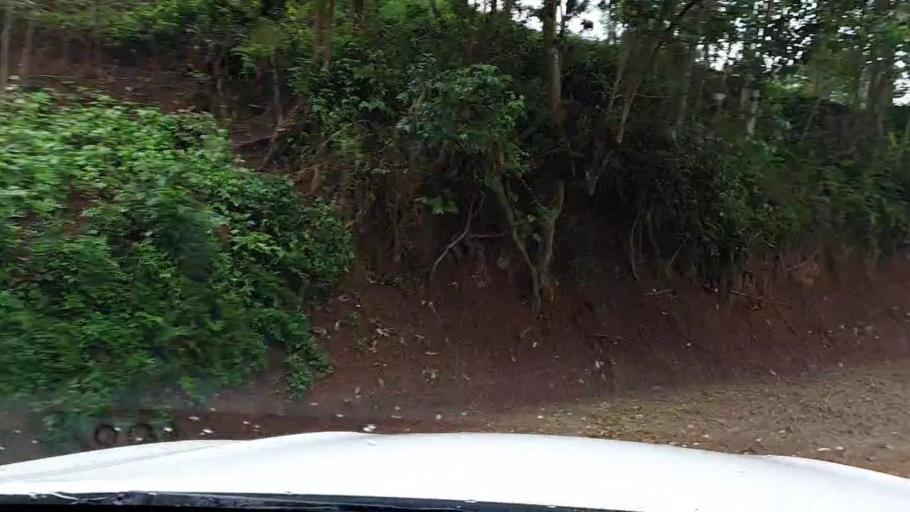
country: RW
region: Western Province
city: Cyangugu
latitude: -2.5436
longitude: 28.9769
